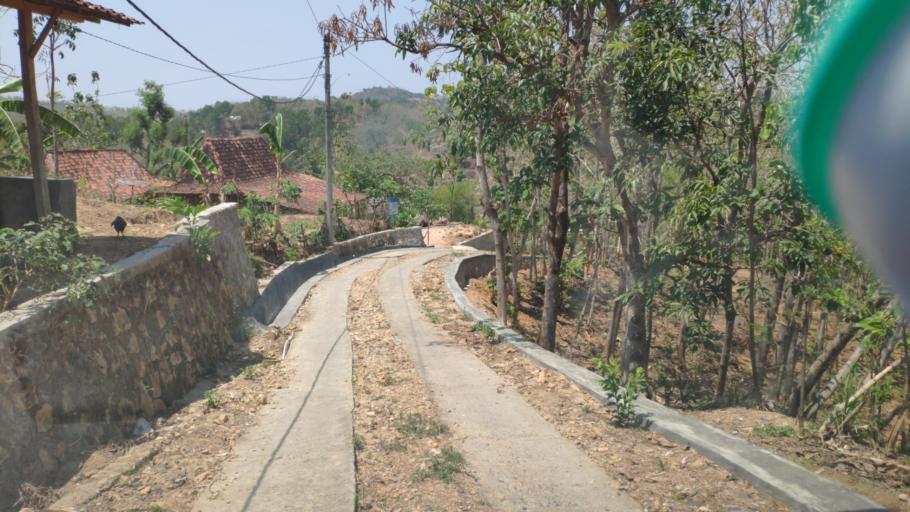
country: ID
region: Central Java
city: Ngapus
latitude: -6.9292
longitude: 111.2060
